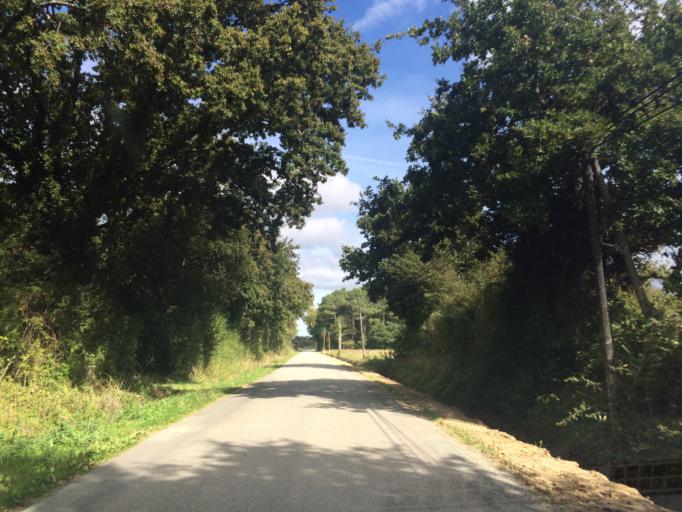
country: FR
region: Pays de la Loire
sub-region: Departement de la Loire-Atlantique
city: Chemere
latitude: 47.1025
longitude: -1.9056
